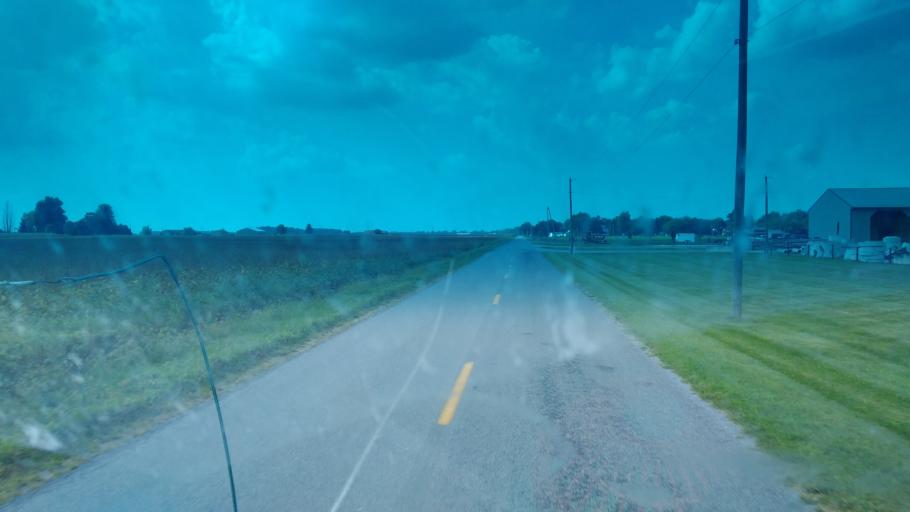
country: US
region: Ohio
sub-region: Hardin County
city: Ada
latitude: 40.7029
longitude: -83.9113
